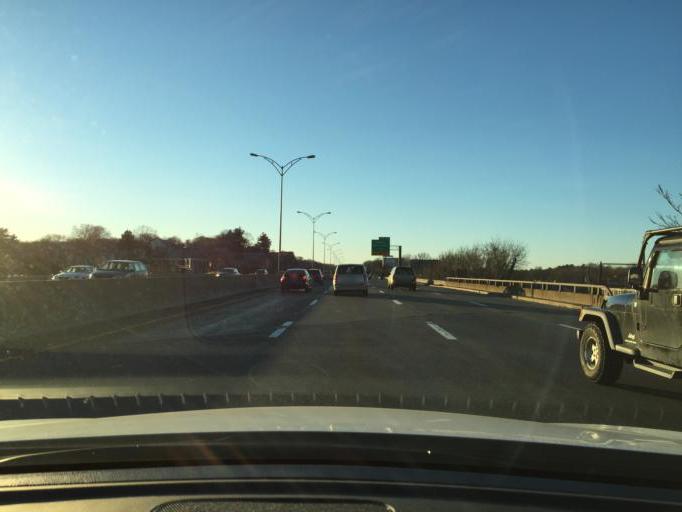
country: US
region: Massachusetts
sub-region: Middlesex County
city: Watertown
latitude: 42.3579
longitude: -71.1537
